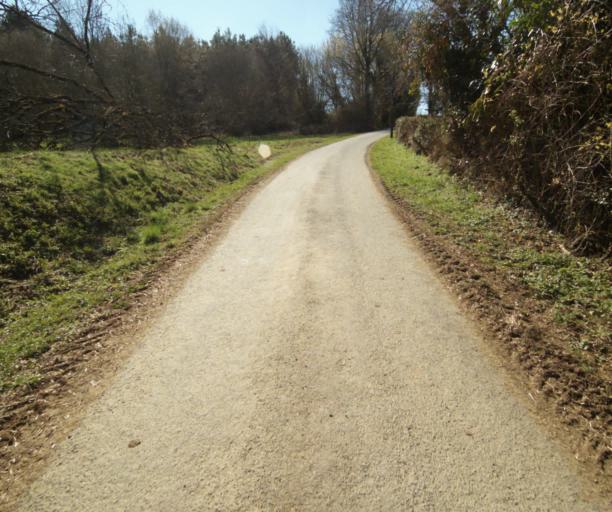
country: FR
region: Limousin
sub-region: Departement de la Correze
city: Chamboulive
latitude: 45.4081
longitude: 1.7297
